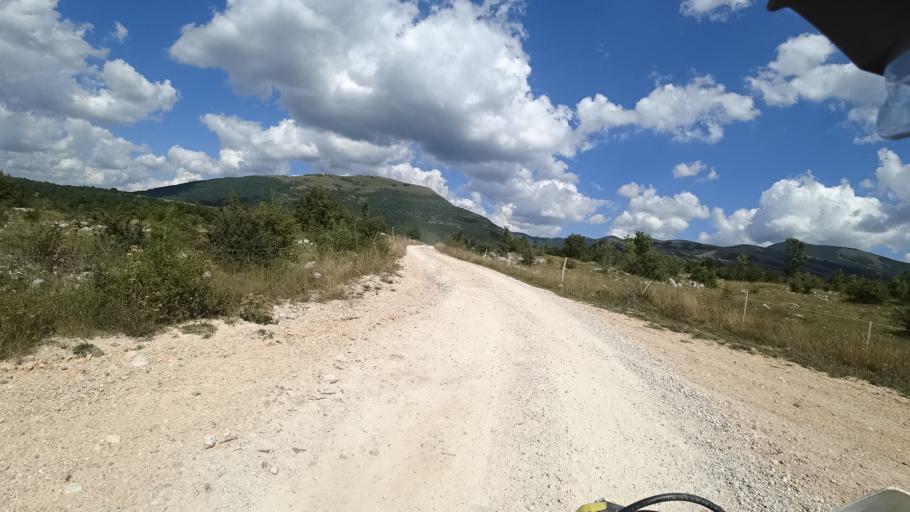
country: HR
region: Zadarska
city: Gracac
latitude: 44.5446
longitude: 15.8133
